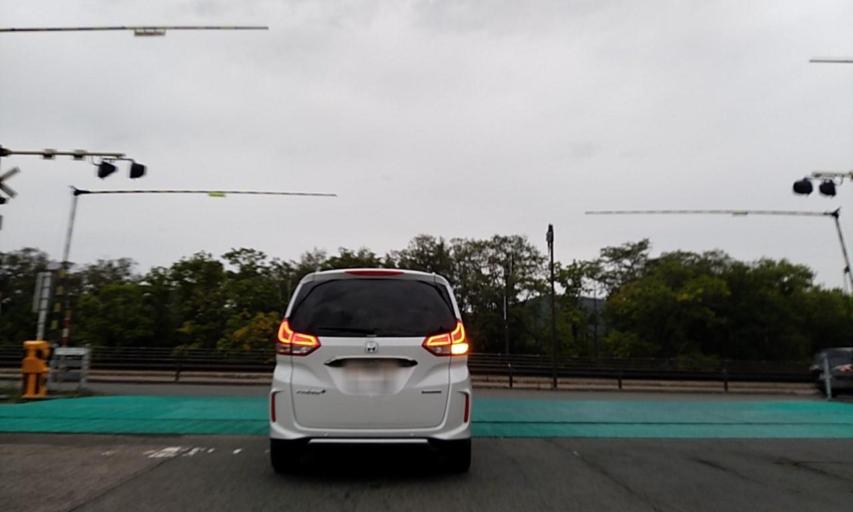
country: JP
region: Hokkaido
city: Abashiri
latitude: 44.0042
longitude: 144.2307
